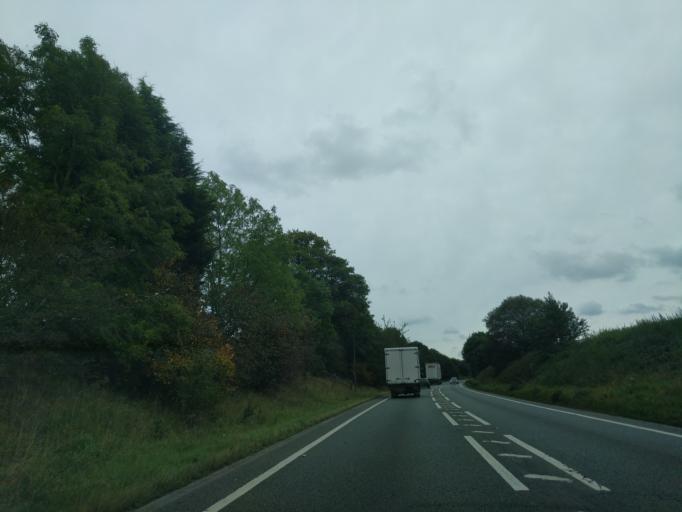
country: GB
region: England
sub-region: Cheshire East
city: Weston
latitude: 53.0728
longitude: -2.3508
